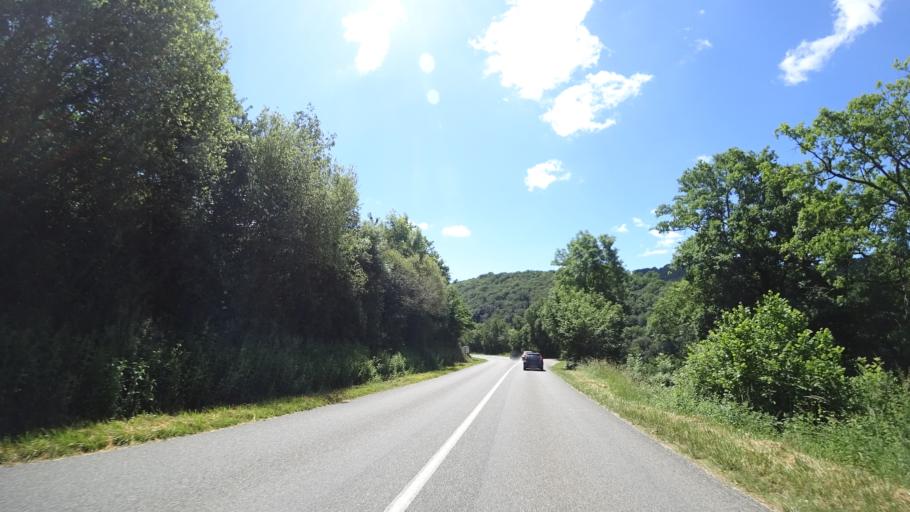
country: FR
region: Midi-Pyrenees
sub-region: Departement de l'Aveyron
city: Colombies
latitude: 44.3808
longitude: 2.3051
